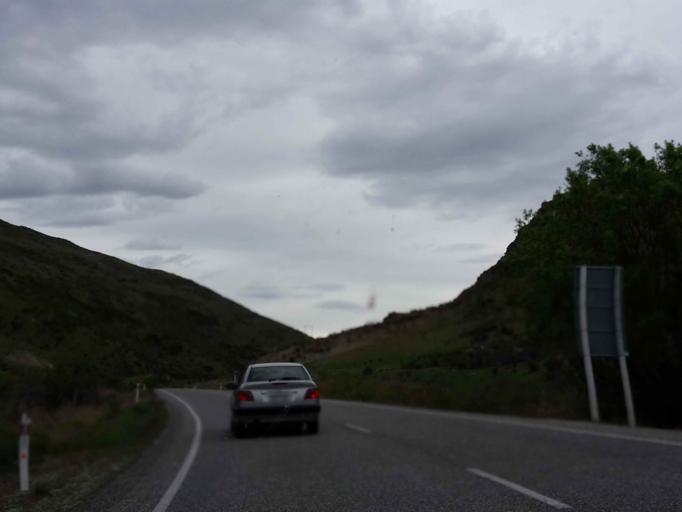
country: NZ
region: Otago
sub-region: Queenstown-Lakes District
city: Wanaka
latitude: -44.7324
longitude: 169.5092
